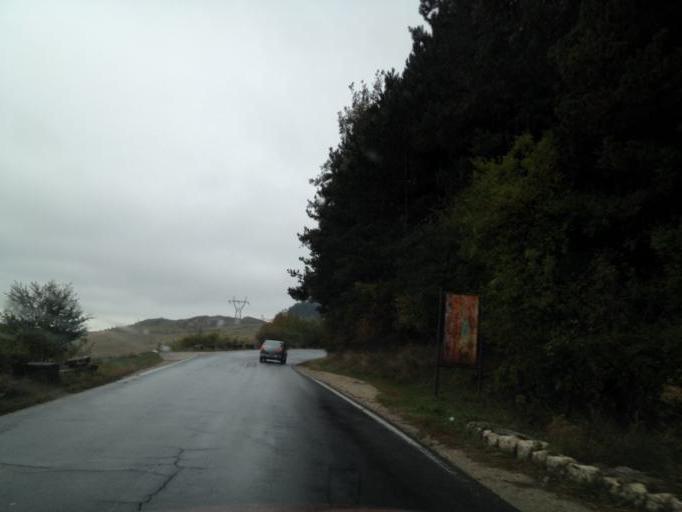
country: RO
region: Arges
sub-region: Comuna Stoenesti
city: Stoenesti
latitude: 45.2976
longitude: 25.1454
